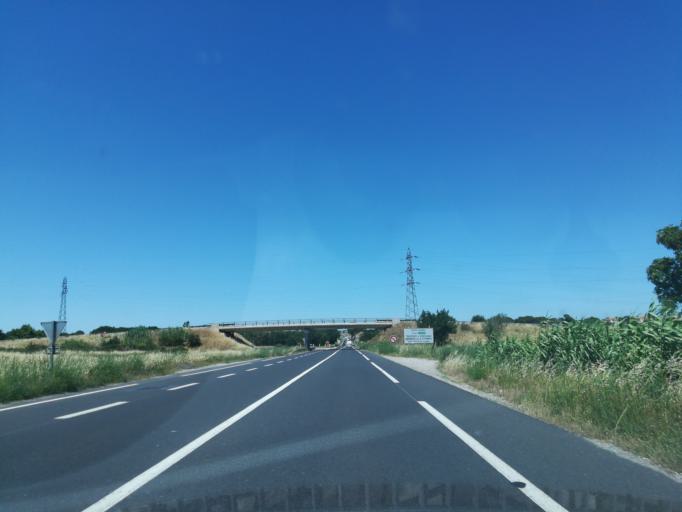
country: FR
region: Languedoc-Roussillon
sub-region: Departement des Pyrenees-Orientales
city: Pollestres
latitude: 42.6568
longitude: 2.8826
